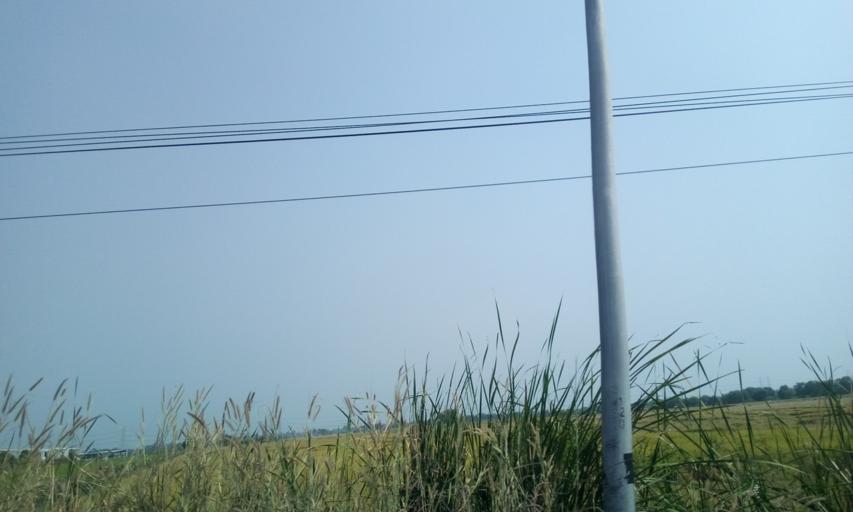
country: TH
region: Pathum Thani
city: Ban Lam Luk Ka
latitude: 13.9833
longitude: 100.7551
